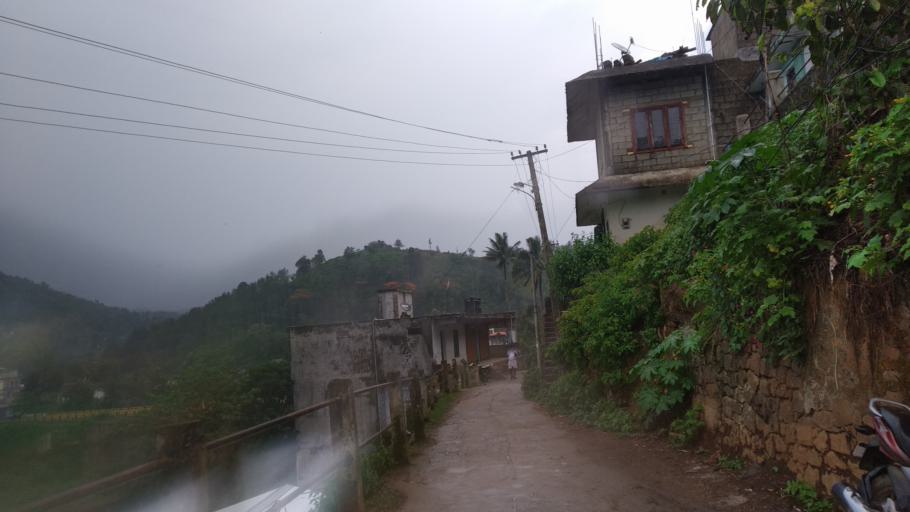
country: IN
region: Tamil Nadu
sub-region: Theni
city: Gudalur
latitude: 9.5715
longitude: 77.0920
